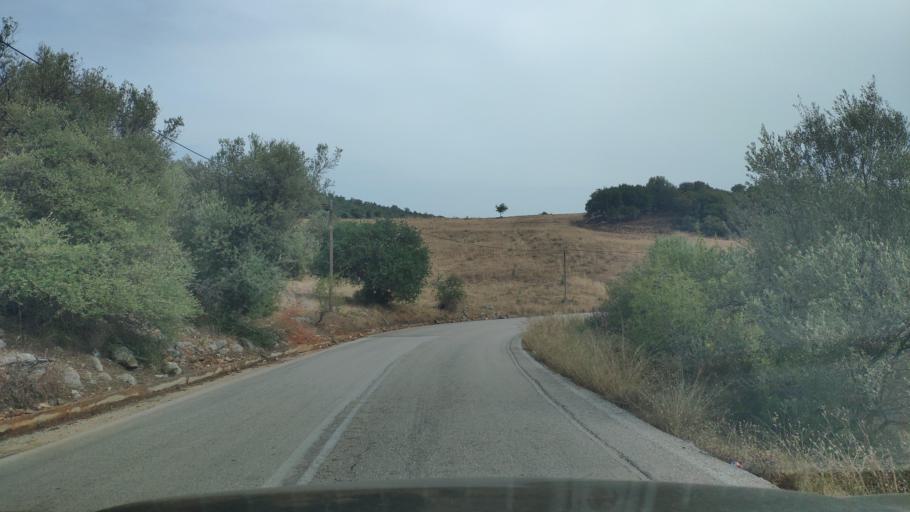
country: GR
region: Peloponnese
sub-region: Nomos Argolidos
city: Palaia Epidavros
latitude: 37.5808
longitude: 23.1545
